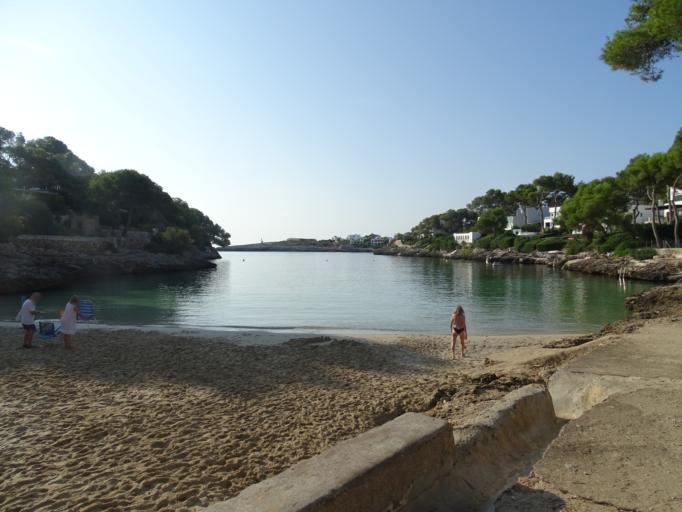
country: ES
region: Balearic Islands
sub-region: Illes Balears
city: Santanyi
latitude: 39.3711
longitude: 3.2299
